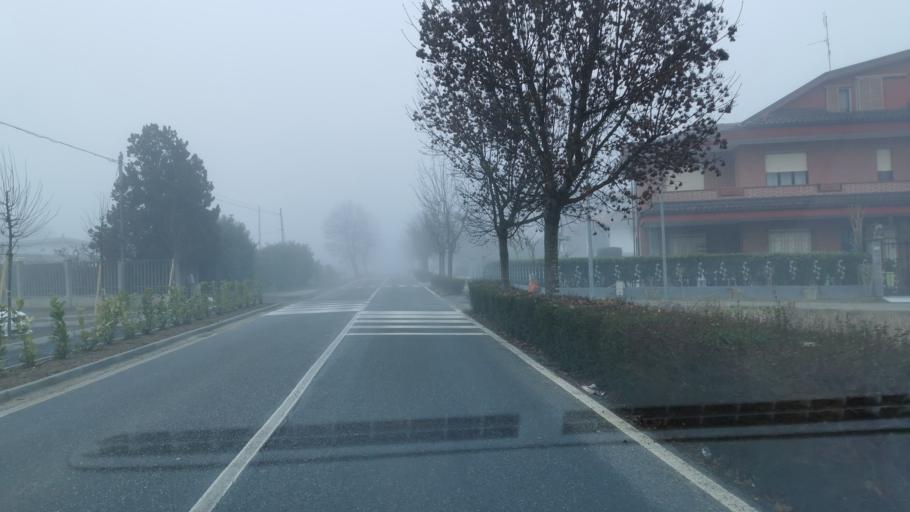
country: IT
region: Piedmont
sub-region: Provincia di Torino
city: Volpiano
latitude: 45.1943
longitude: 7.7585
